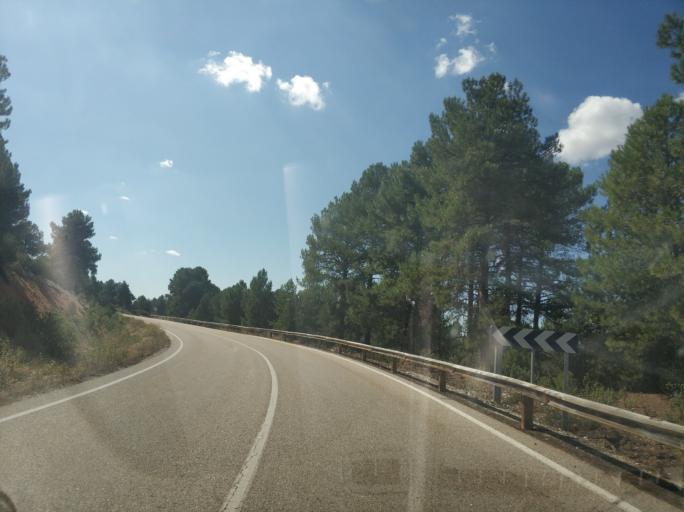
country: ES
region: Castille and Leon
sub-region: Provincia de Soria
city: Herrera de Soria
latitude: 41.7496
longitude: -3.0402
